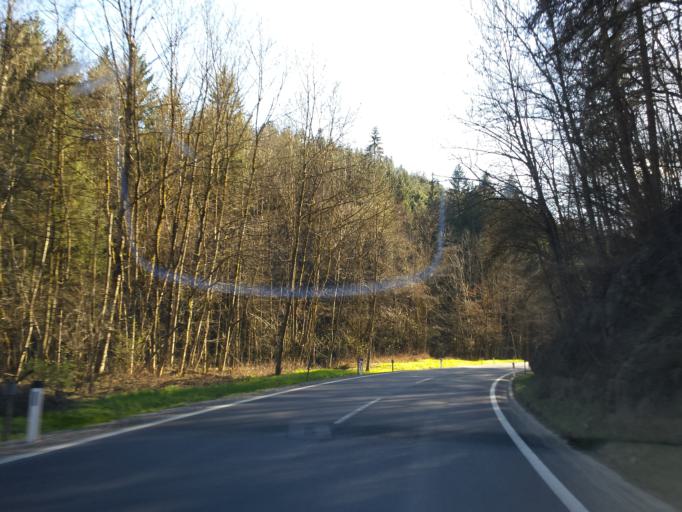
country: AT
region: Styria
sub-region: Politischer Bezirk Graz-Umgebung
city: Sankt Radegund bei Graz
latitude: 47.1366
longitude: 15.4711
